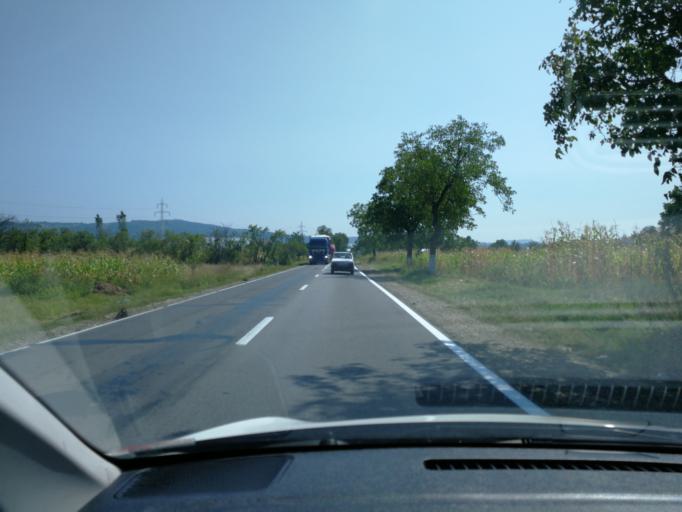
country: RO
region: Prahova
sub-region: Comuna Izvoarele
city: Homoraciu
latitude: 45.2439
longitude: 26.0261
